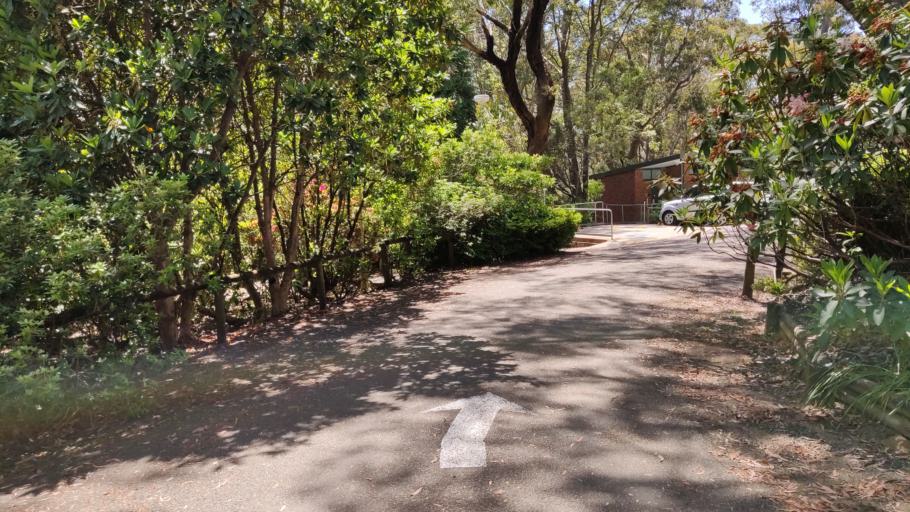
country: AU
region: New South Wales
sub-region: Blue Mountains Municipality
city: Blackheath
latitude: -33.6271
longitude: 150.2883
